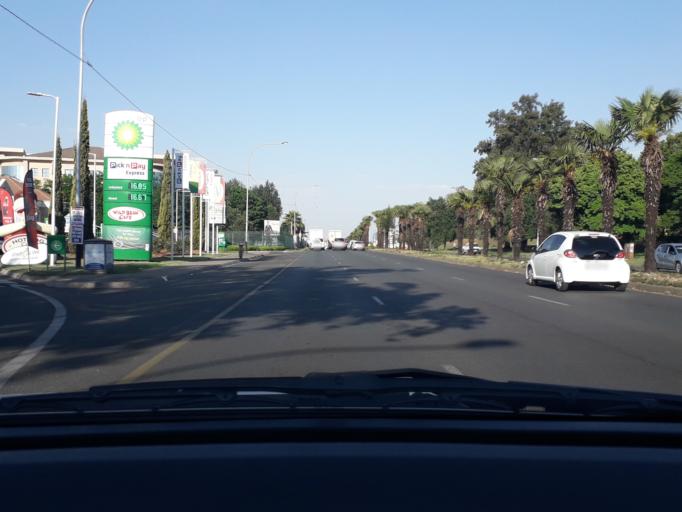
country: ZA
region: Gauteng
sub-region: City of Johannesburg Metropolitan Municipality
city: Johannesburg
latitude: -26.1834
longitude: 28.1070
